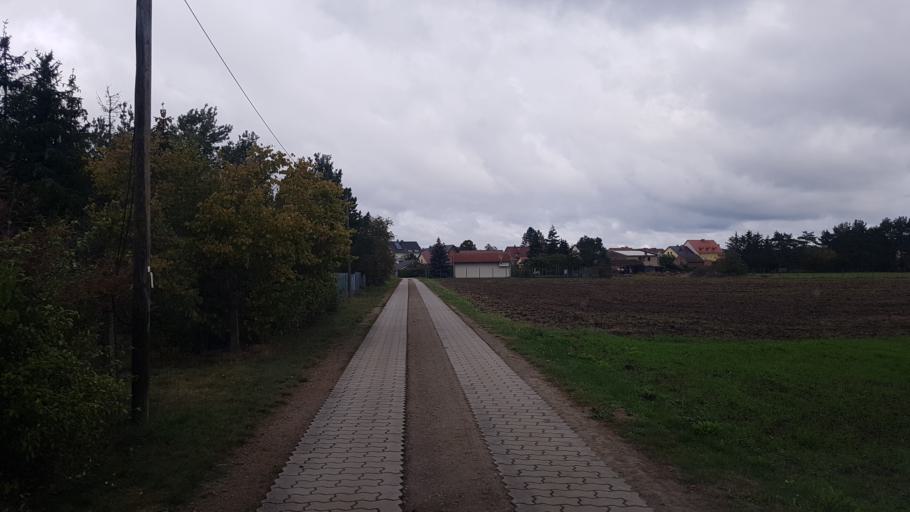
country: DE
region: Brandenburg
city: Altdobern
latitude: 51.6461
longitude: 14.0268
